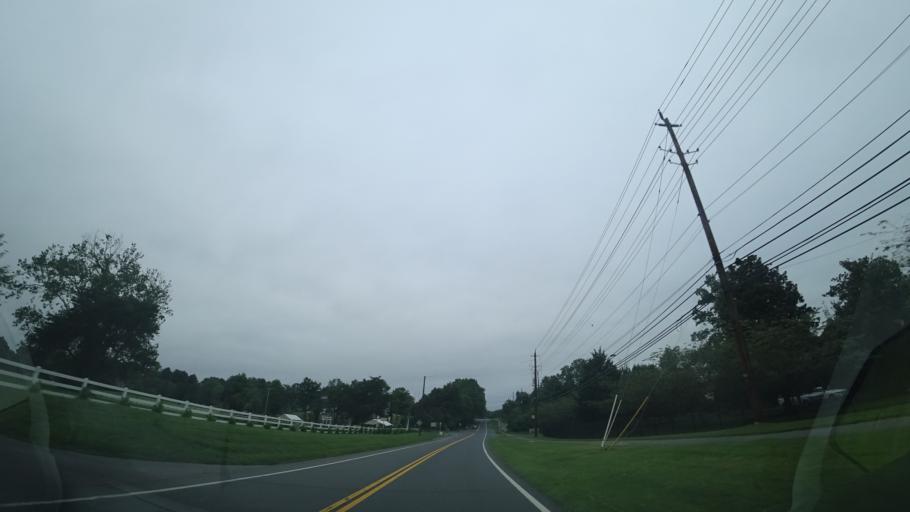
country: US
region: Maryland
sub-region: Montgomery County
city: Potomac
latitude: 39.0060
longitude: -77.1898
